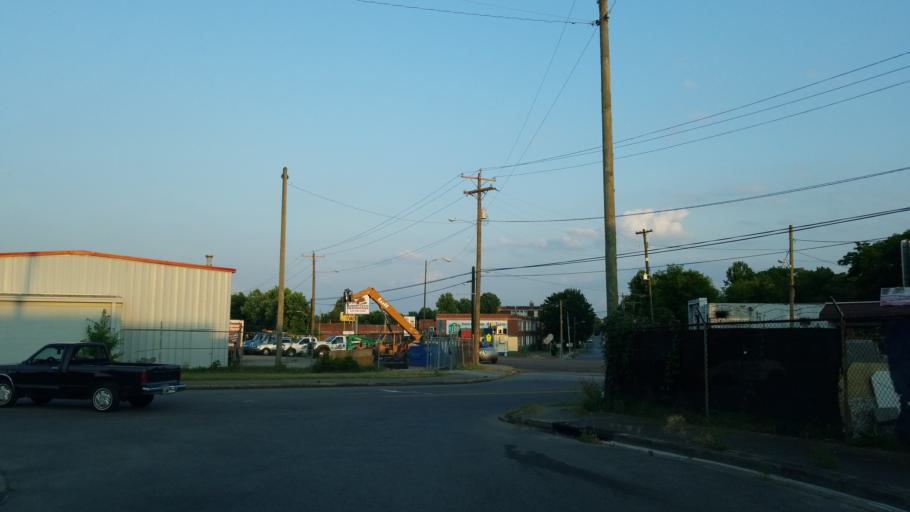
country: US
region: Tennessee
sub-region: Davidson County
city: Nashville
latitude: 36.1504
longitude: -86.7660
